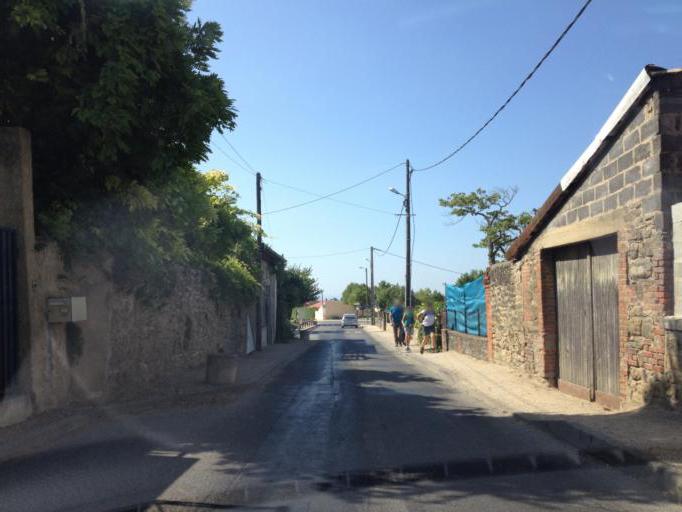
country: FR
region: Rhone-Alpes
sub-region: Departement de la Drome
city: Clerieux
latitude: 45.1349
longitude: 4.9481
